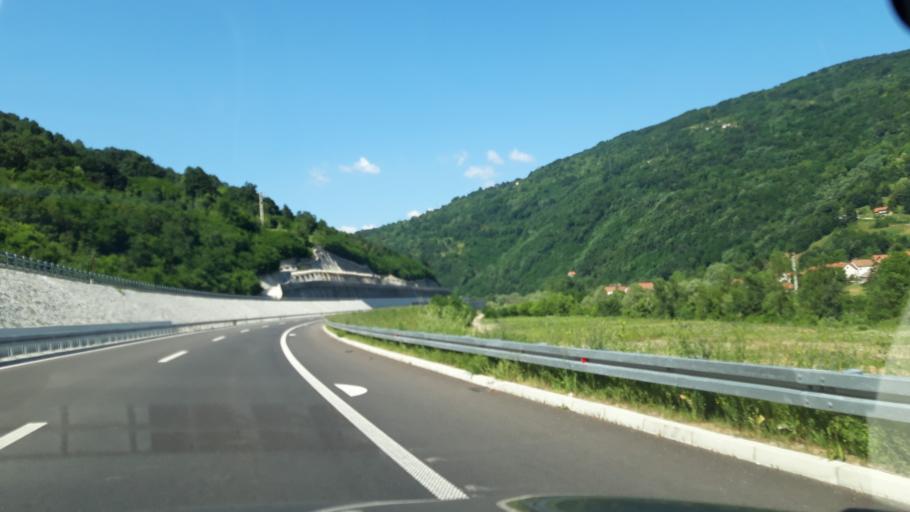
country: RS
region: Central Serbia
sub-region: Pcinjski Okrug
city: Vladicin Han
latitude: 42.7735
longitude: 22.0862
